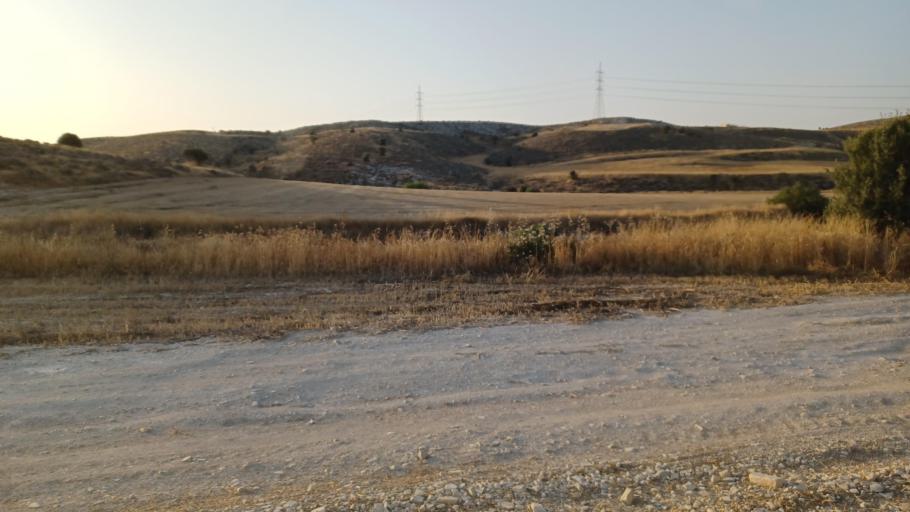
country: CY
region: Larnaka
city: Athienou
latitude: 34.9948
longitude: 33.5334
